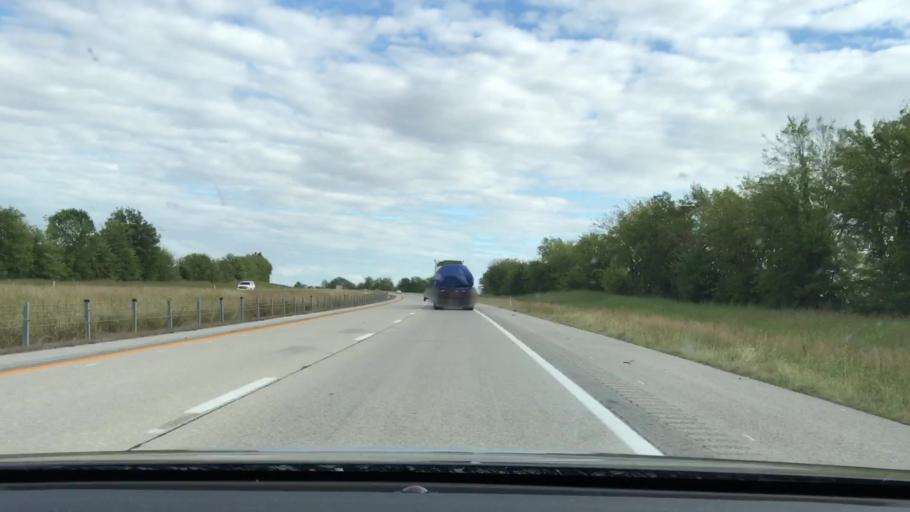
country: US
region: Kentucky
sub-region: Christian County
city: Hopkinsville
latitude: 36.7955
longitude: -87.6040
